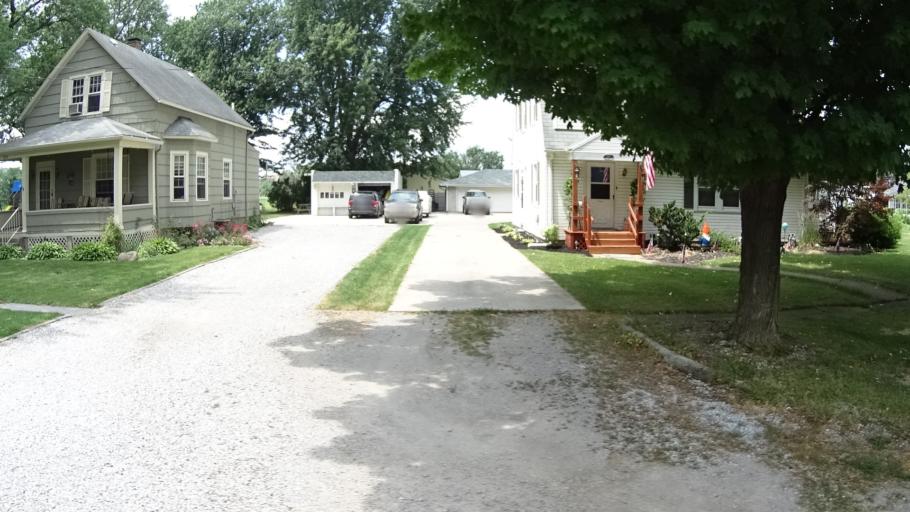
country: US
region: Ohio
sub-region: Erie County
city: Sandusky
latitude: 41.4459
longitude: -82.7719
